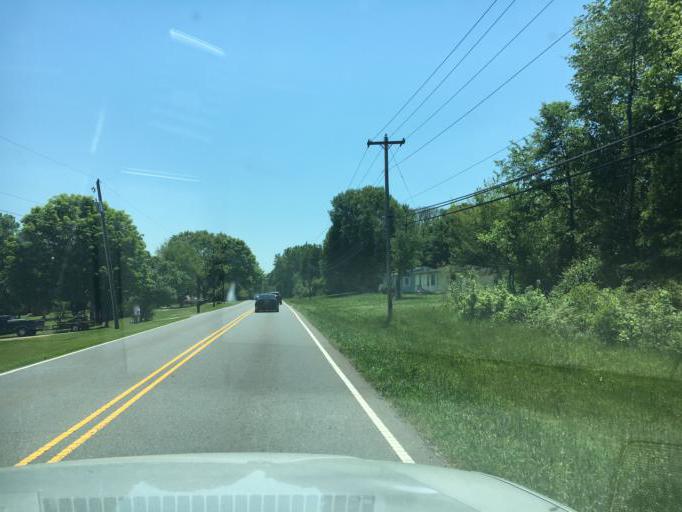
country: US
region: North Carolina
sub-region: Cleveland County
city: Shelby
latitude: 35.2515
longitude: -81.5662
